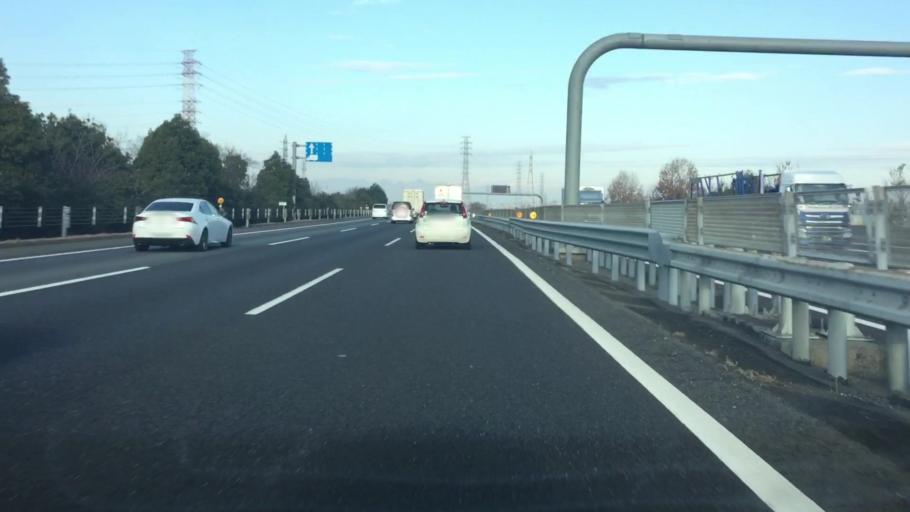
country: JP
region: Saitama
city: Honjo
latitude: 36.2217
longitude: 139.1618
